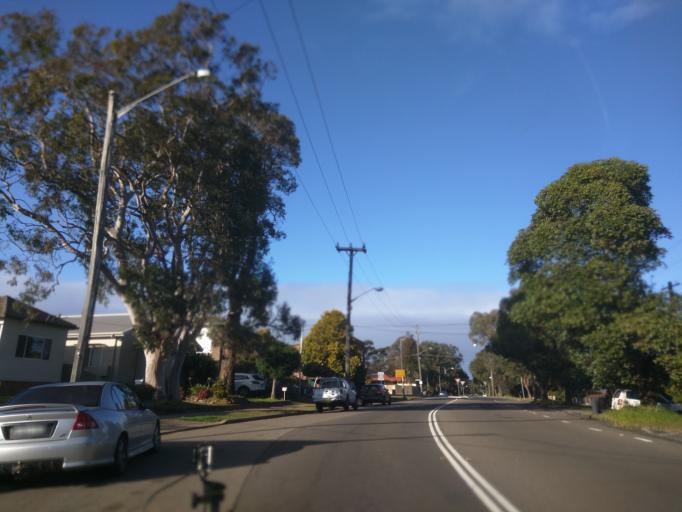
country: AU
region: New South Wales
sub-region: Hurstville
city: Peakhurst
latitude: -33.9661
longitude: 151.0498
